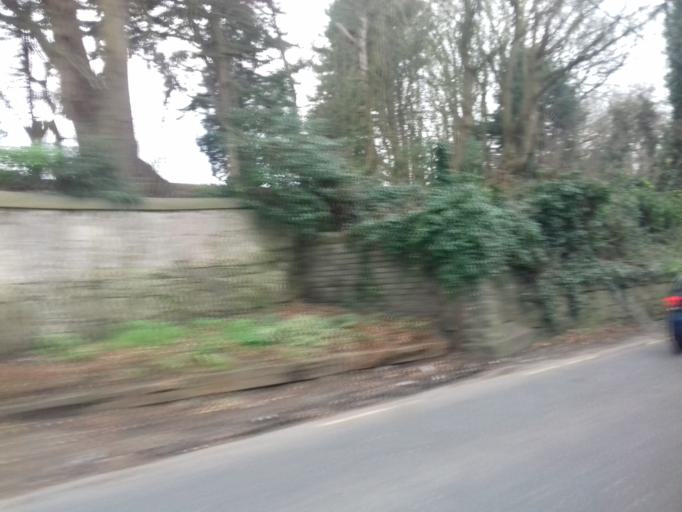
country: IE
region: Leinster
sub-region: Lu
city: Drogheda
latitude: 53.7107
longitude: -6.3351
